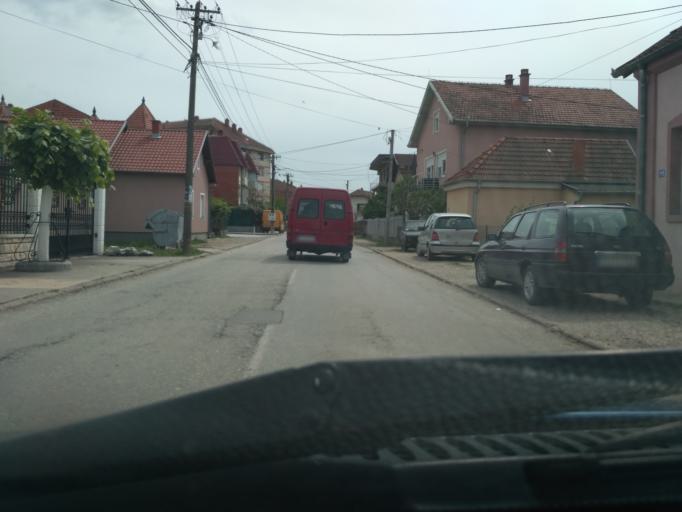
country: RS
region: Central Serbia
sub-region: Pomoravski Okrug
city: Svilajnac
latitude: 44.2358
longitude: 21.1933
